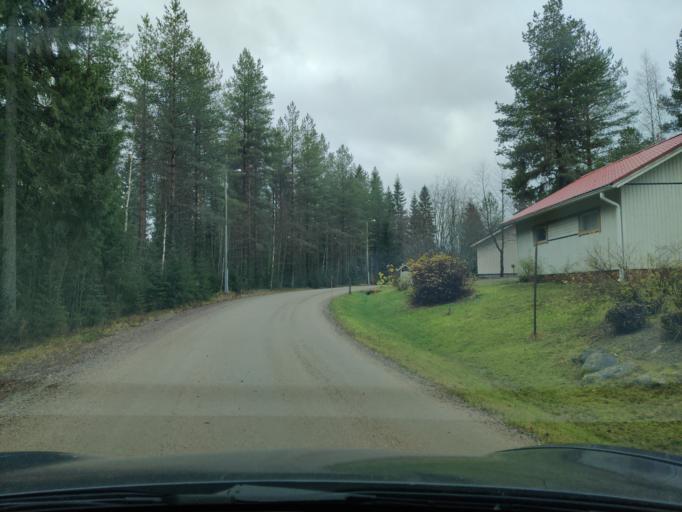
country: FI
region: Northern Savo
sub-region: Ylae-Savo
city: Kiuruvesi
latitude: 63.6425
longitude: 26.6403
